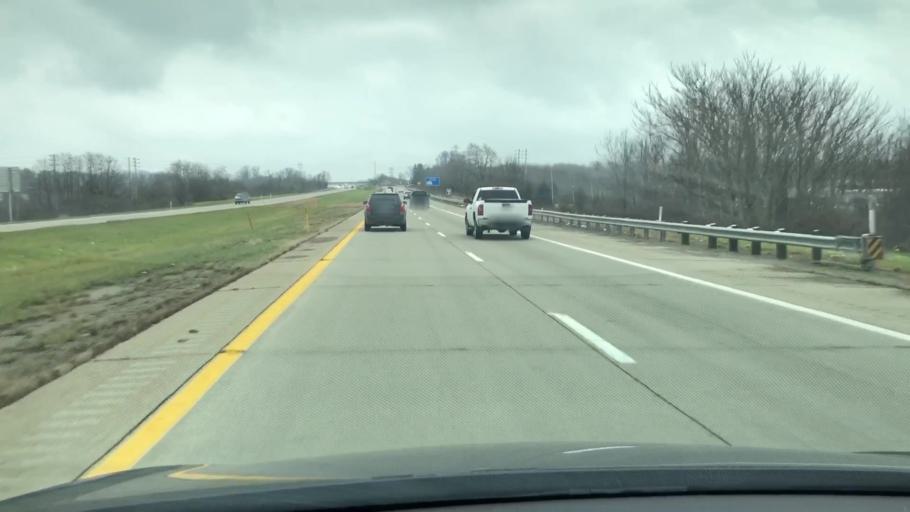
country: US
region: Pennsylvania
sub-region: Westmoreland County
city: Mount Pleasant
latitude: 40.1874
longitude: -79.5686
